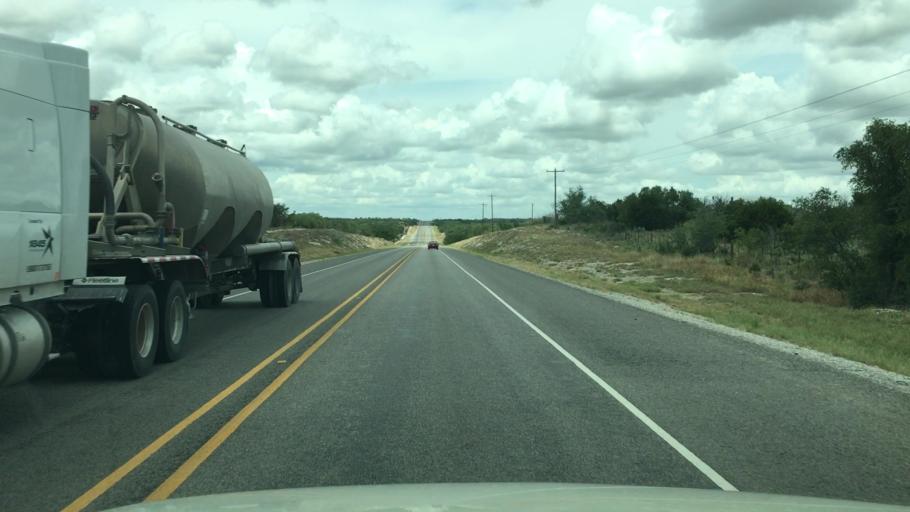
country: US
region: Texas
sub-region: McCulloch County
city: Brady
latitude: 31.0371
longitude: -99.2379
